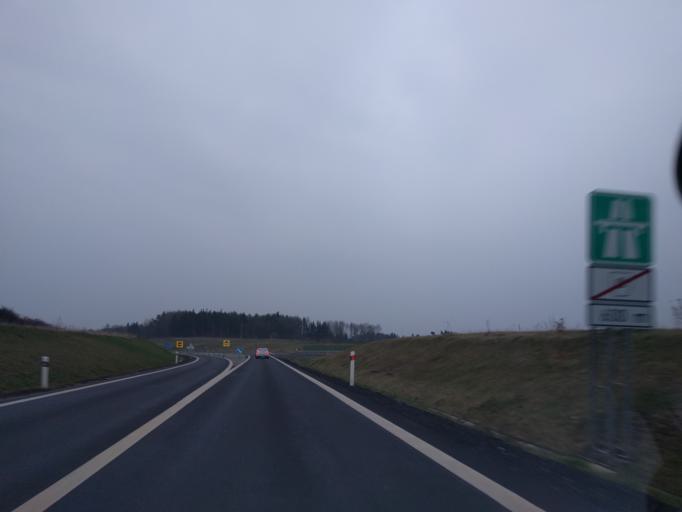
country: CZ
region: Karlovarsky
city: Zlutice
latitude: 50.1345
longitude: 13.2258
